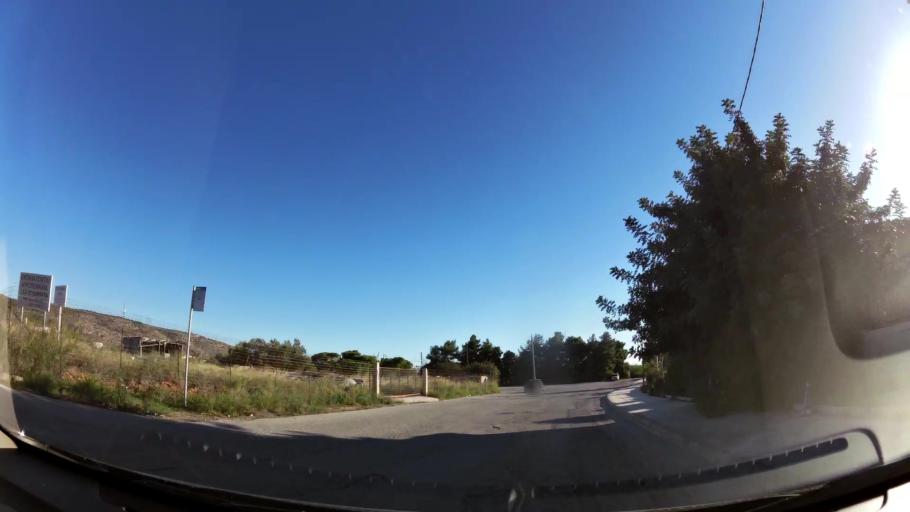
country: GR
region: Attica
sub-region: Nomarchia Anatolikis Attikis
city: Vari
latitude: 37.8300
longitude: 23.8059
